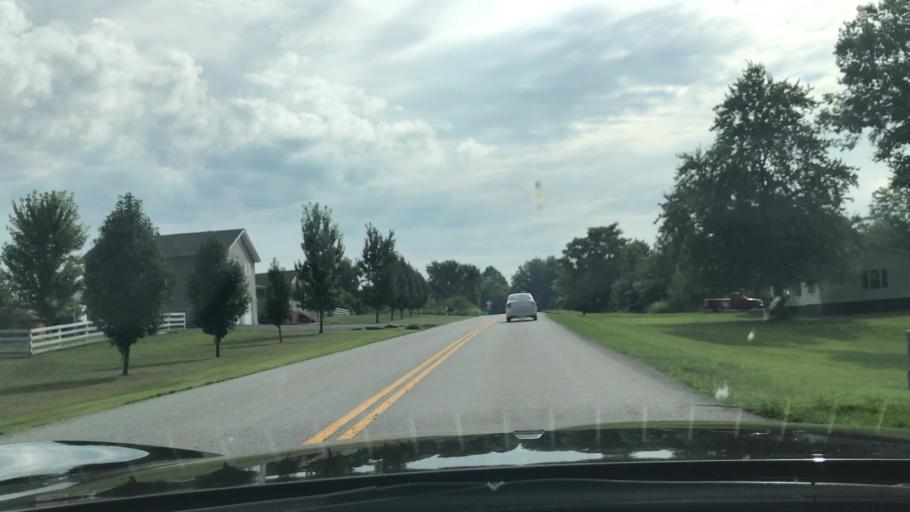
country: US
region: Kentucky
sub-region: Green County
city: Greensburg
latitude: 37.2674
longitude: -85.5428
